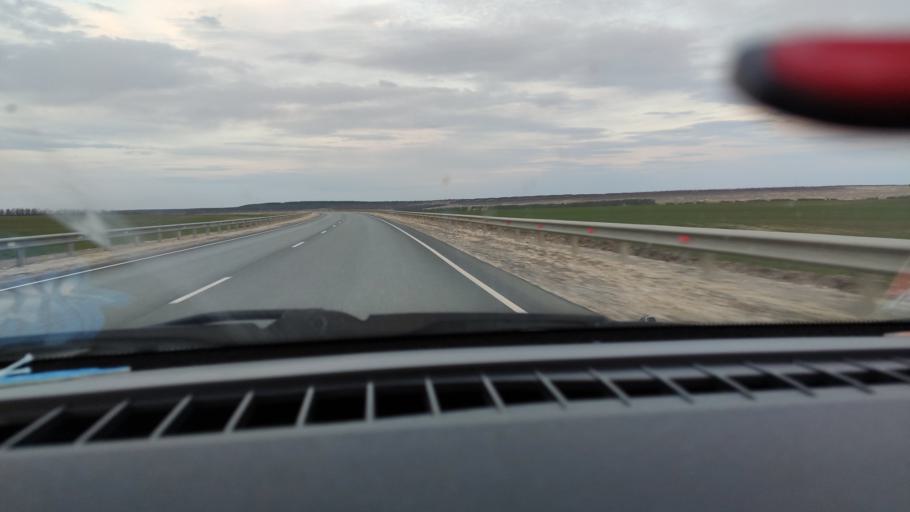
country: RU
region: Saratov
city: Yelshanka
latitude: 51.8334
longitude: 46.4653
